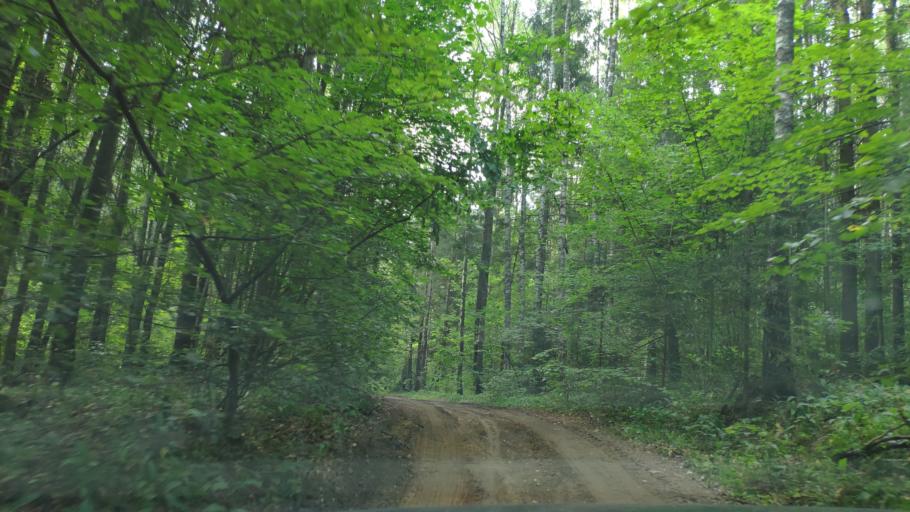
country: BY
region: Minsk
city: Zaslawye
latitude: 53.9660
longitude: 27.2971
